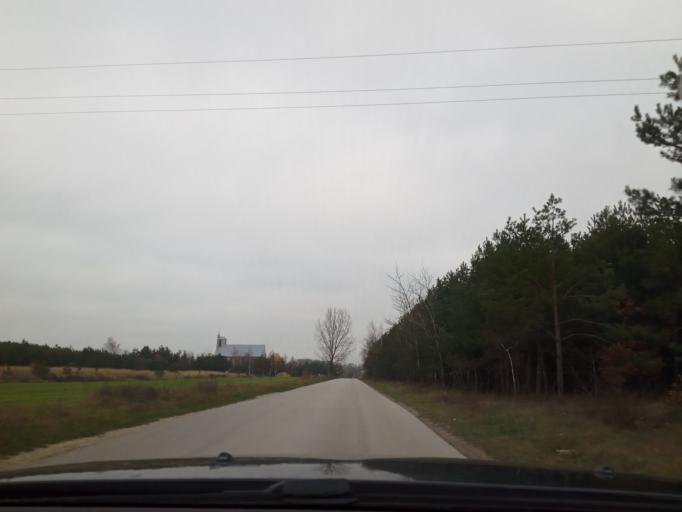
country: PL
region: Swietokrzyskie
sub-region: Powiat jedrzejowski
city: Imielno
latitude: 50.5983
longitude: 20.4839
